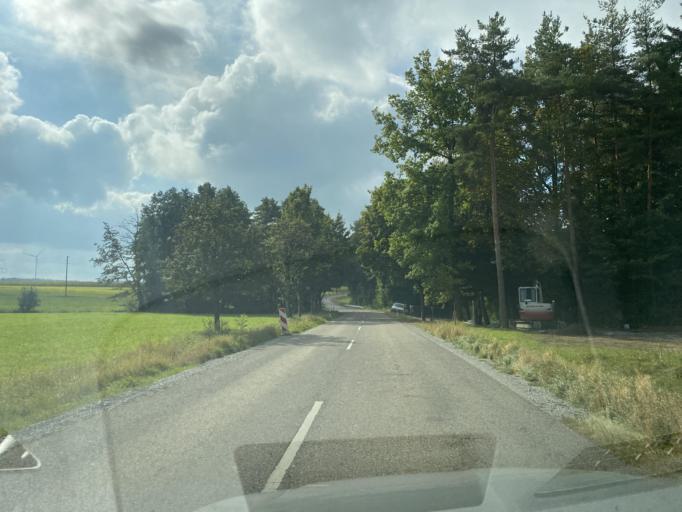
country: DE
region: Baden-Wuerttemberg
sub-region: Regierungsbezirk Stuttgart
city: Buhlertann
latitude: 49.0466
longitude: 9.9589
